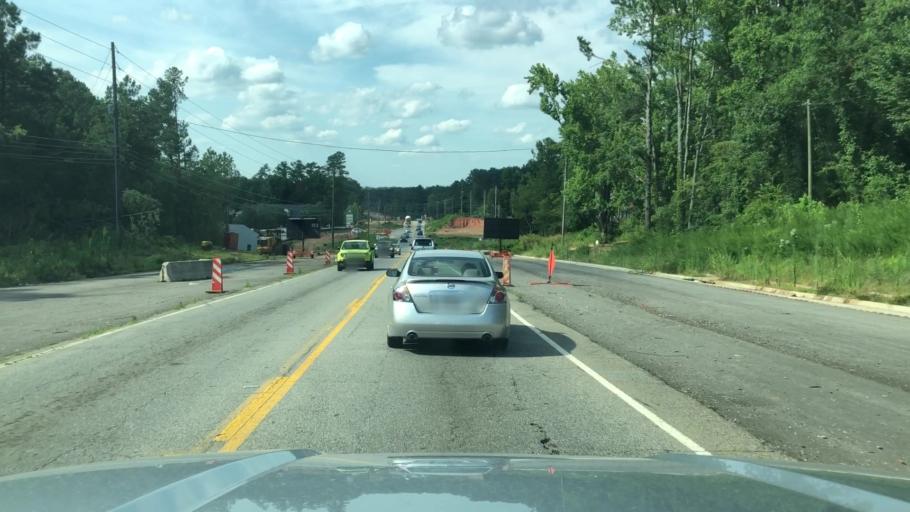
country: US
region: Georgia
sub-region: Douglas County
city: Douglasville
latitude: 33.7710
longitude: -84.7479
